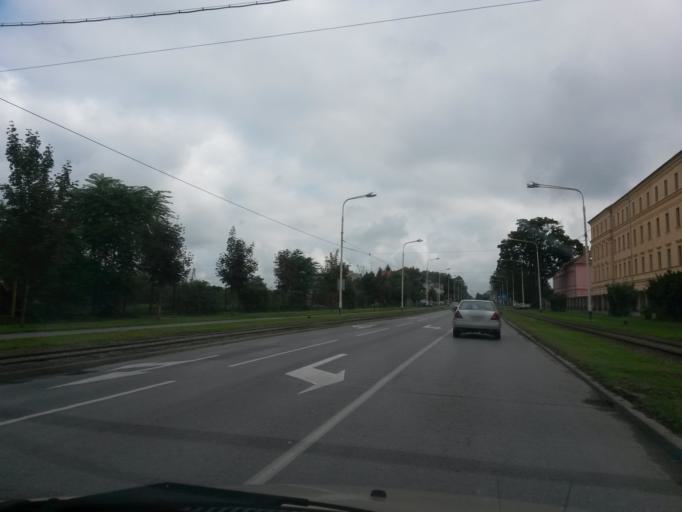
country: HR
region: Osjecko-Baranjska
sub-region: Grad Osijek
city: Osijek
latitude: 45.5585
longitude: 18.7056
